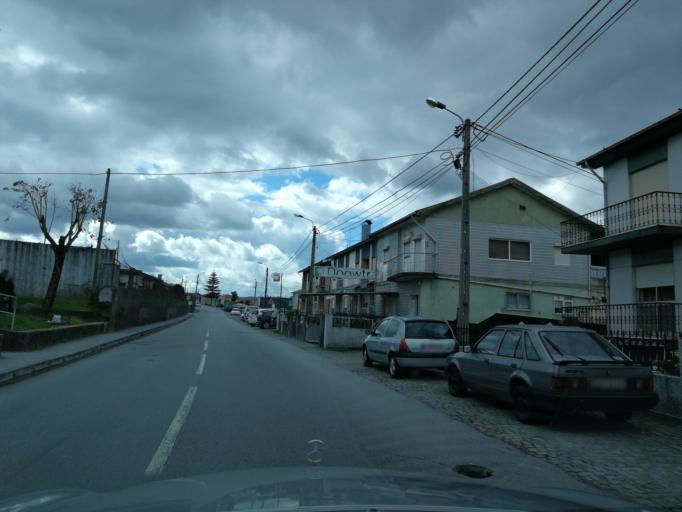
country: PT
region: Braga
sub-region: Braga
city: Braga
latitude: 41.5375
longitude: -8.4292
